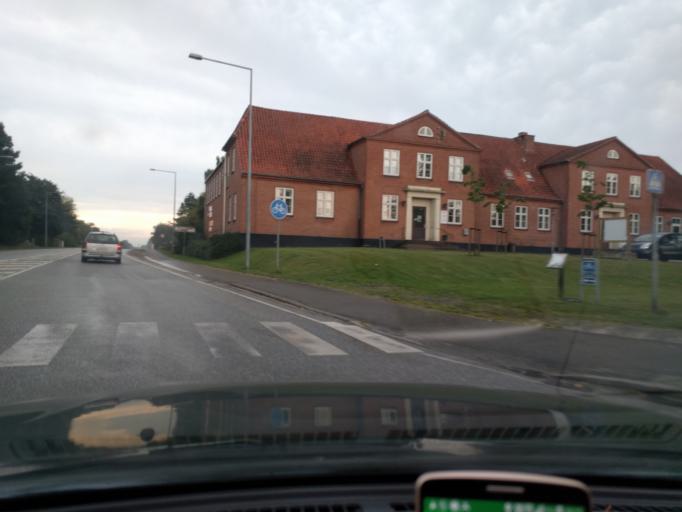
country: DK
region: Zealand
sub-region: Guldborgsund Kommune
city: Norre Alslev
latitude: 54.8999
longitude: 11.8727
